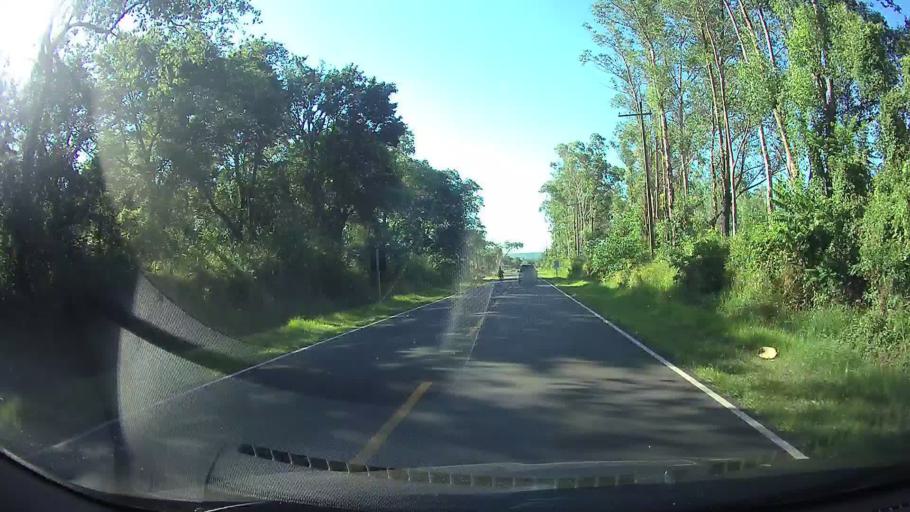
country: PY
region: Cordillera
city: Atyra
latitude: -25.3036
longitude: -57.1586
